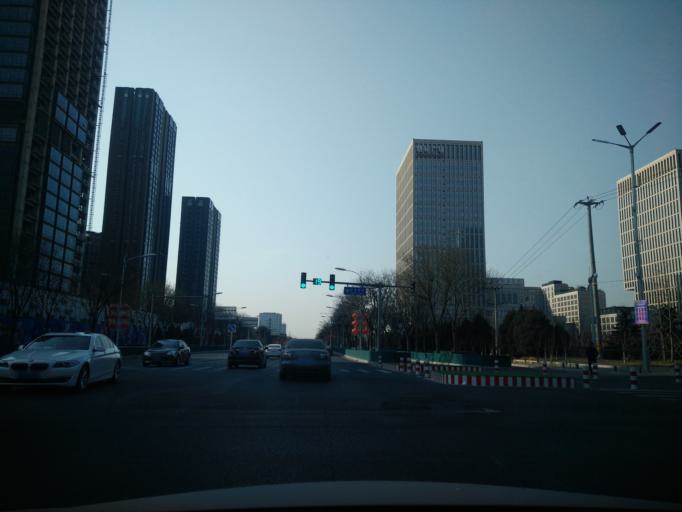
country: CN
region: Beijing
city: Jiugong
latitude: 39.7917
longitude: 116.5038
